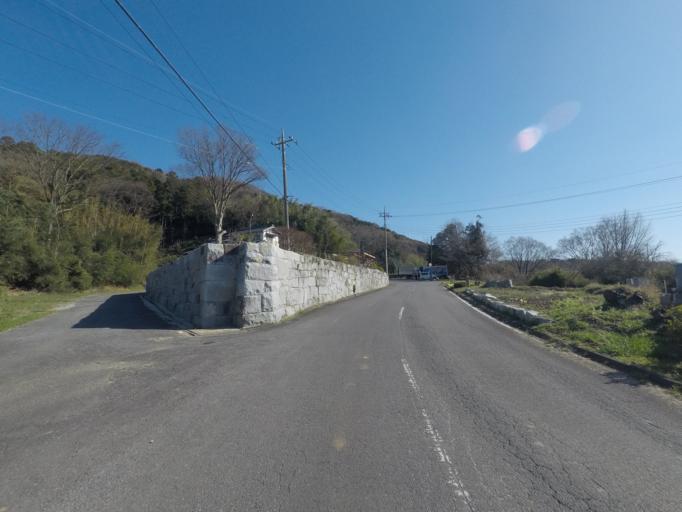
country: JP
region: Ibaraki
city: Makabe
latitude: 36.2416
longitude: 140.0724
